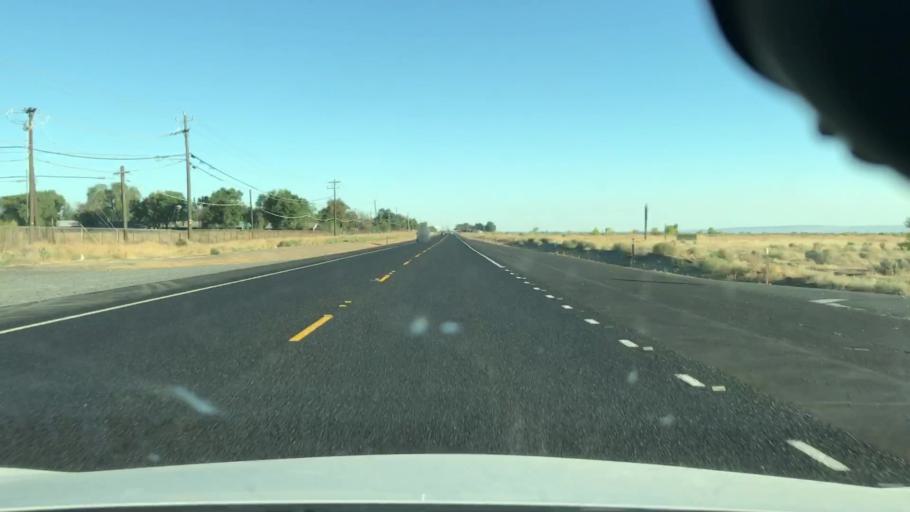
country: US
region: Washington
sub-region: Grant County
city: Moses Lake North
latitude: 47.1735
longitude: -119.3300
